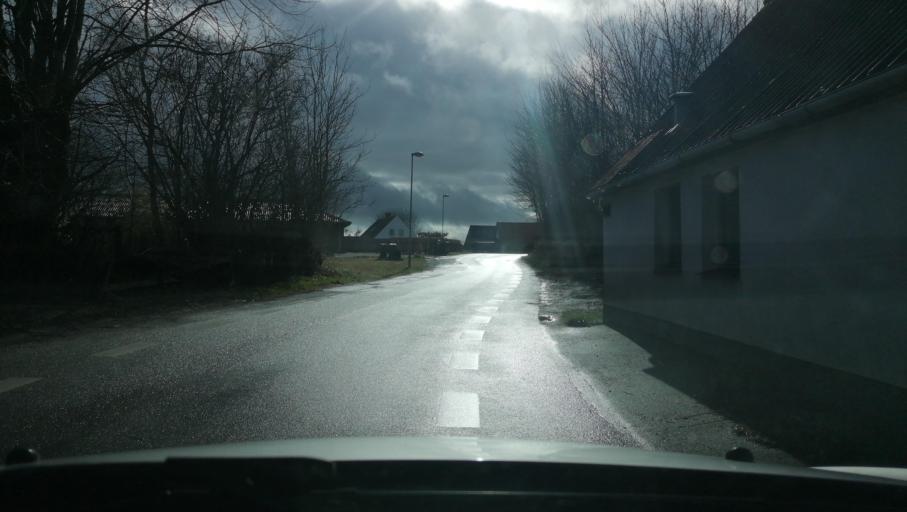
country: DK
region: Zealand
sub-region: Odsherred Kommune
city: Horve
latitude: 55.7401
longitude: 11.4011
